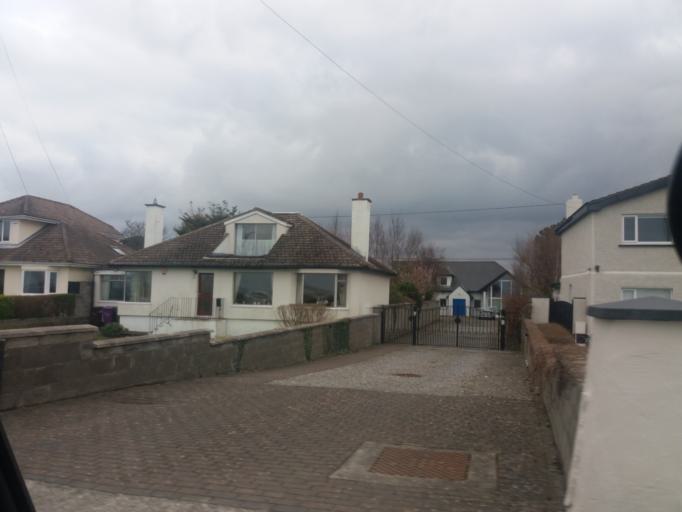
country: IE
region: Leinster
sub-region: Fingal County
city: Baldoyle
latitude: 53.3952
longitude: -6.1239
